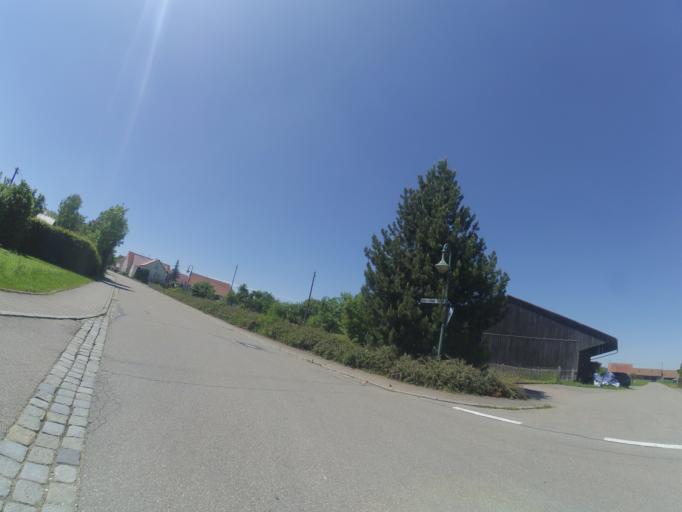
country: DE
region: Baden-Wuerttemberg
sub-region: Tuebingen Region
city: Blaubeuren
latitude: 48.4642
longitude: 9.8454
